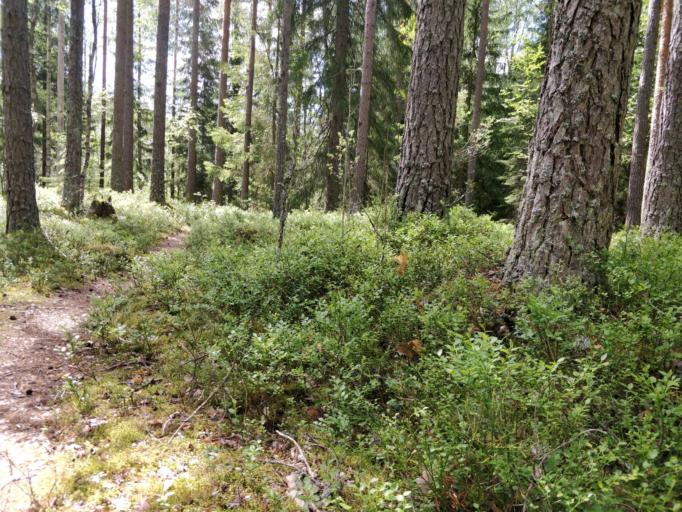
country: FI
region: Uusimaa
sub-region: Helsinki
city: Vihti
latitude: 60.3135
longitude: 24.4699
